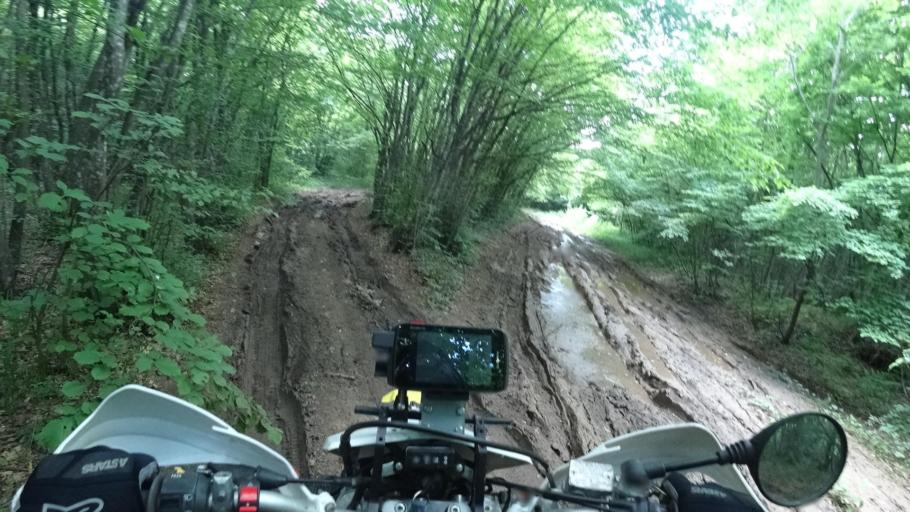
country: BA
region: Federation of Bosnia and Herzegovina
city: Bihac
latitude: 44.8115
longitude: 15.9266
